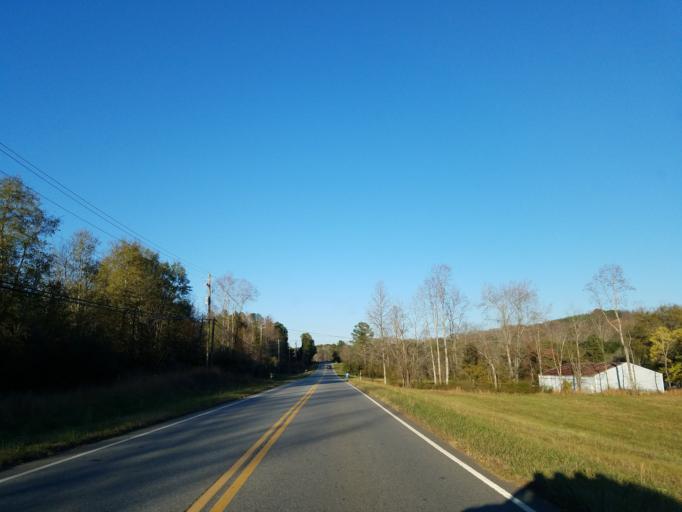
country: US
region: Georgia
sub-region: Cherokee County
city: Ball Ground
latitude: 34.3186
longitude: -84.3957
